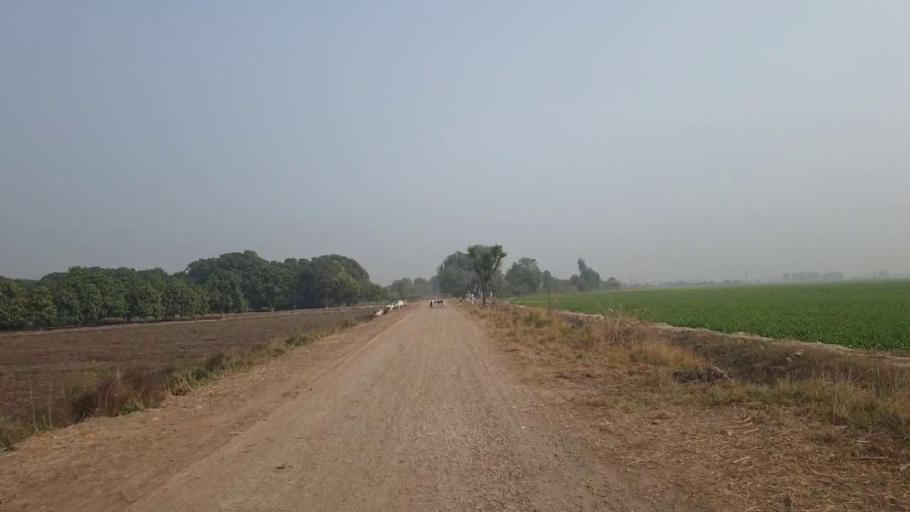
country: PK
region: Sindh
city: Tando Adam
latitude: 25.8203
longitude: 68.5930
